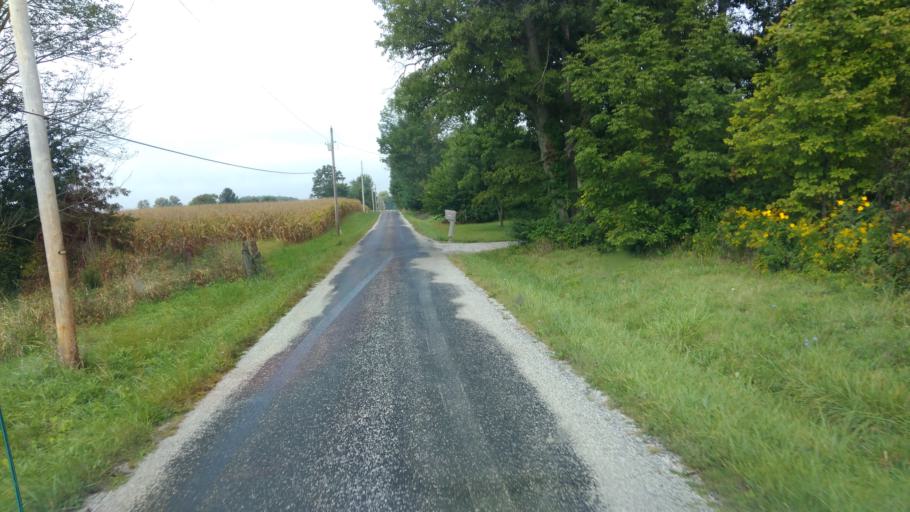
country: US
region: Ohio
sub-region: Morrow County
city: Cardington
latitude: 40.5505
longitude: -82.9787
